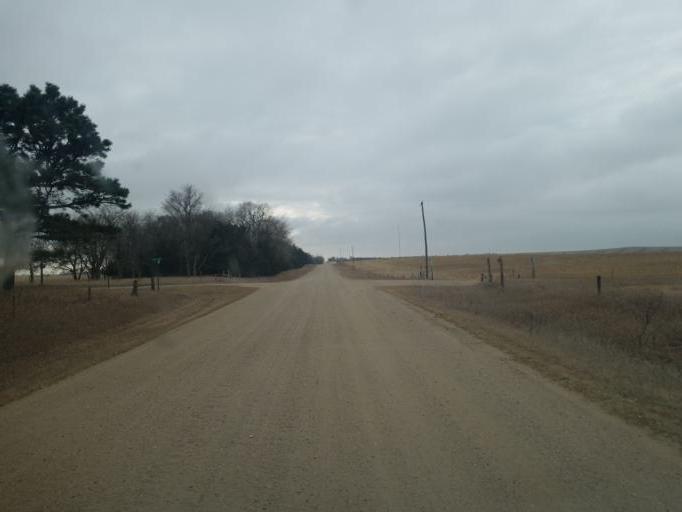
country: US
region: Nebraska
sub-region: Pierce County
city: Plainview
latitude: 42.4239
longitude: -97.7960
